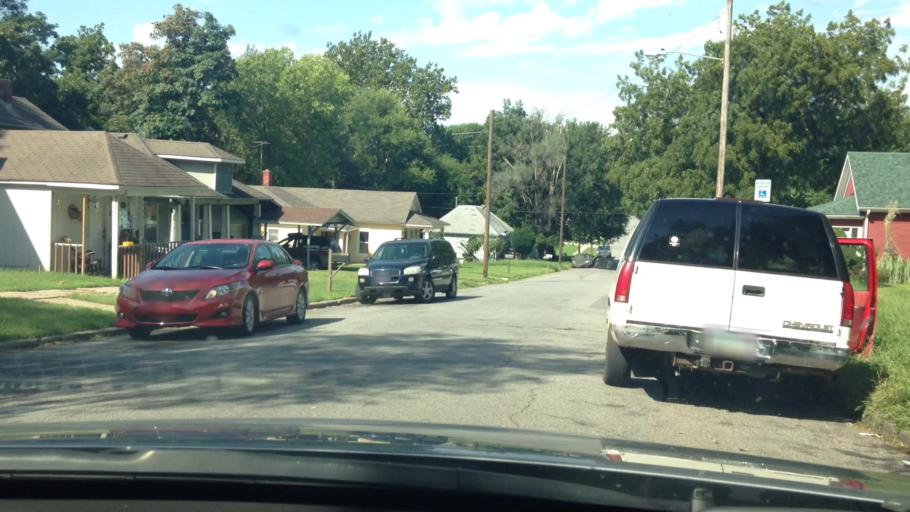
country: US
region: Kansas
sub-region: Leavenworth County
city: Leavenworth
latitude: 39.3232
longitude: -94.9245
